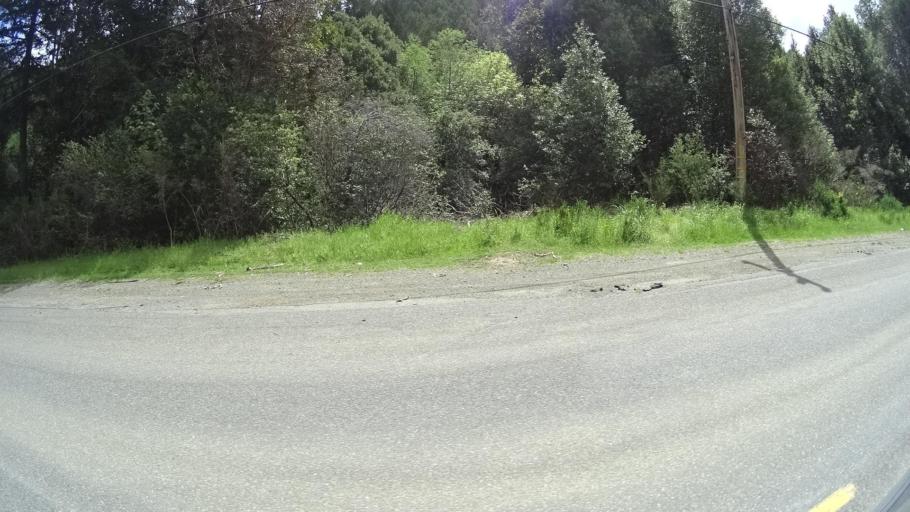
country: US
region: California
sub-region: Humboldt County
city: Redway
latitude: 40.0772
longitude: -123.9560
